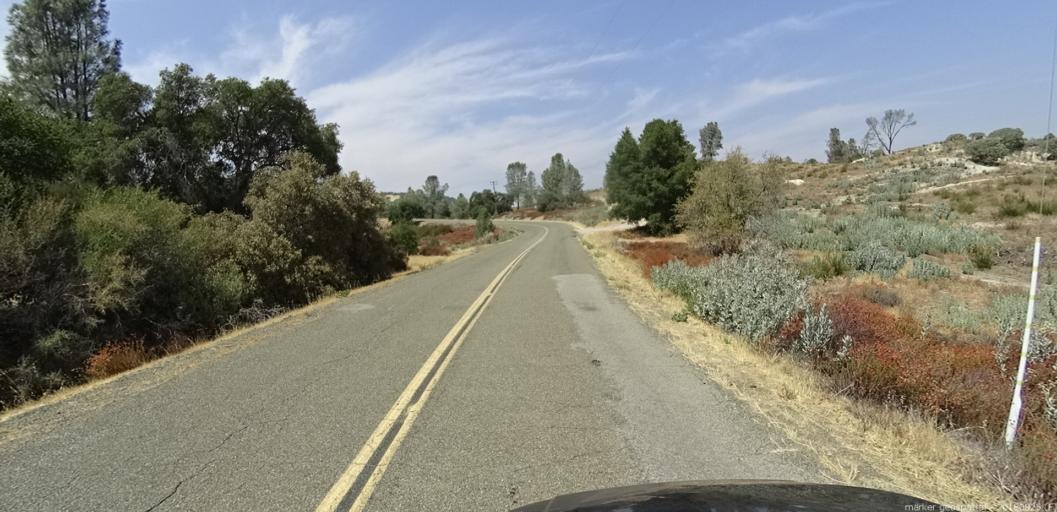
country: US
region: California
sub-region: San Luis Obispo County
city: San Miguel
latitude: 35.9206
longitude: -120.5226
